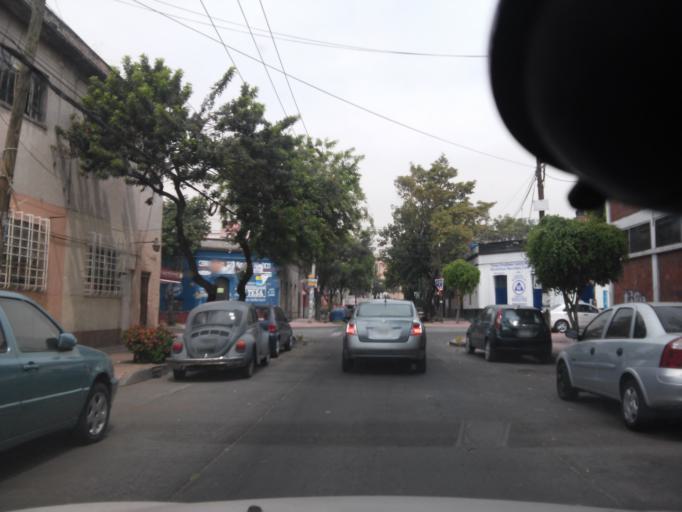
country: MX
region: Mexico City
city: Cuauhtemoc
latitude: 19.4426
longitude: -99.1689
